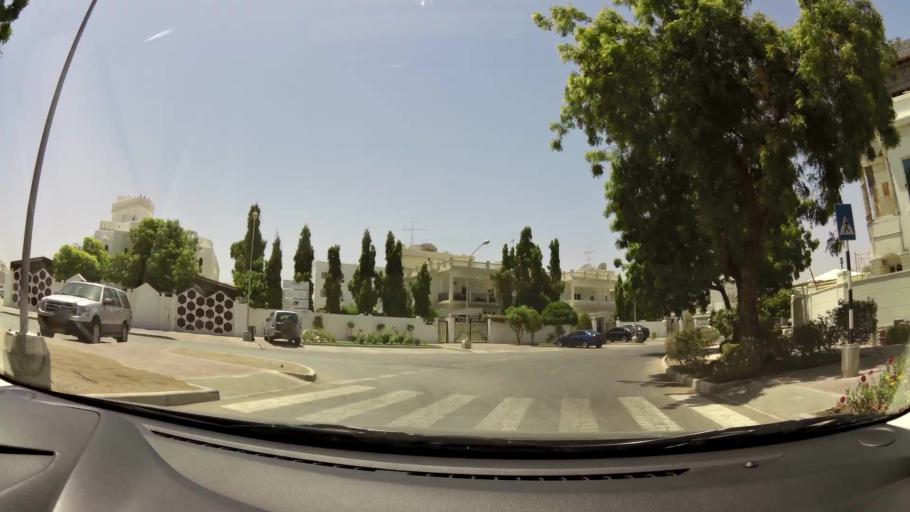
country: OM
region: Muhafazat Masqat
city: Bawshar
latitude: 23.6065
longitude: 58.4449
